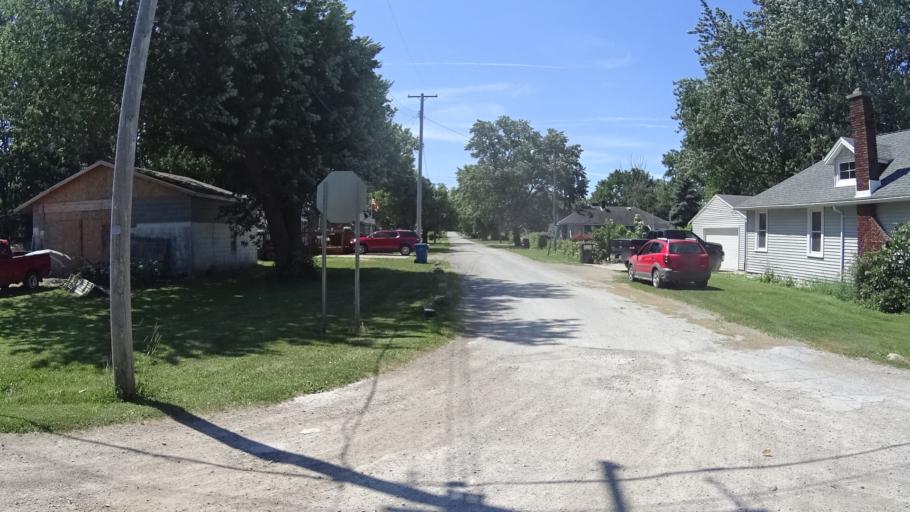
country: US
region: Ohio
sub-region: Ottawa County
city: Port Clinton
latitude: 41.4488
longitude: -82.8442
